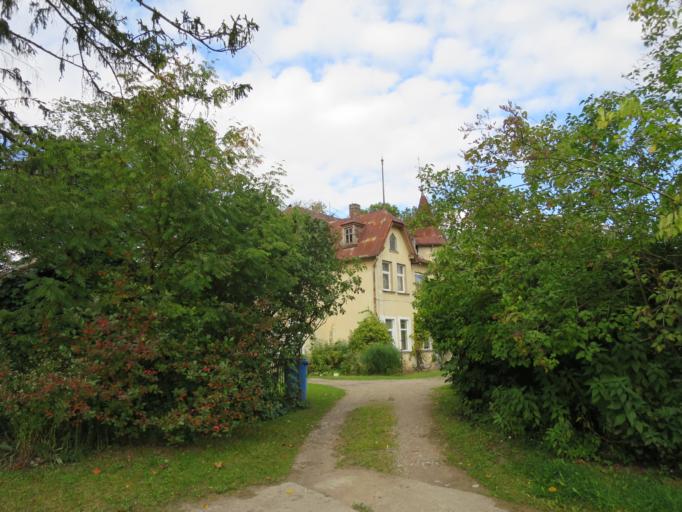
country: LV
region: Sigulda
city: Sigulda
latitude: 57.1545
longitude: 24.8468
